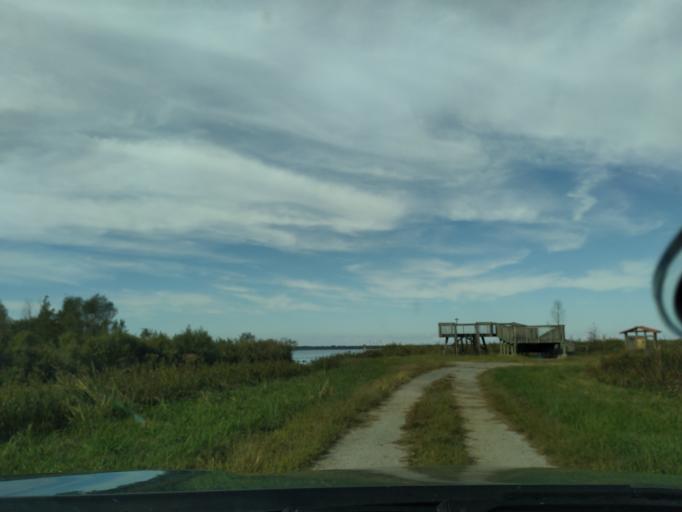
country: US
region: North Carolina
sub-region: Beaufort County
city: Belhaven
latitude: 35.6926
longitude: -76.5422
